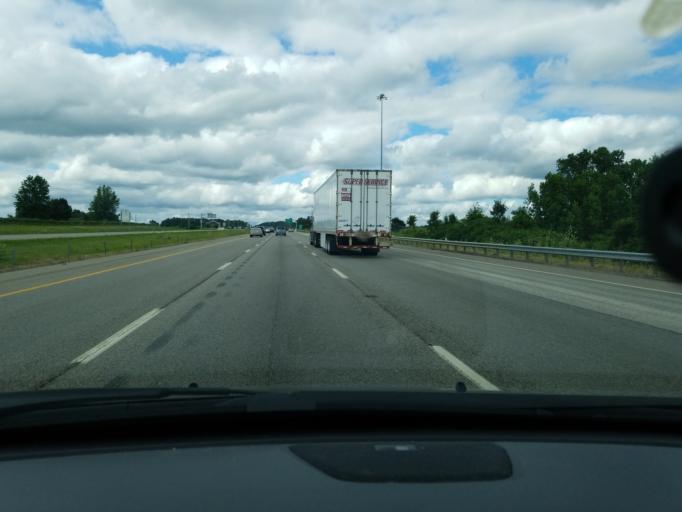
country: US
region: Ohio
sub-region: Stark County
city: Greentown
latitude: 40.9036
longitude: -81.4290
